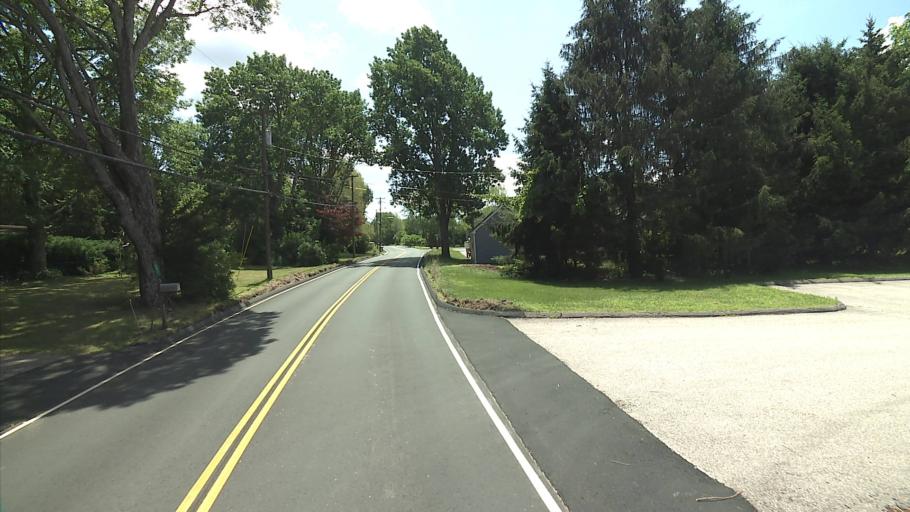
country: US
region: Connecticut
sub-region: New London County
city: Jewett City
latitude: 41.5779
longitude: -71.8972
